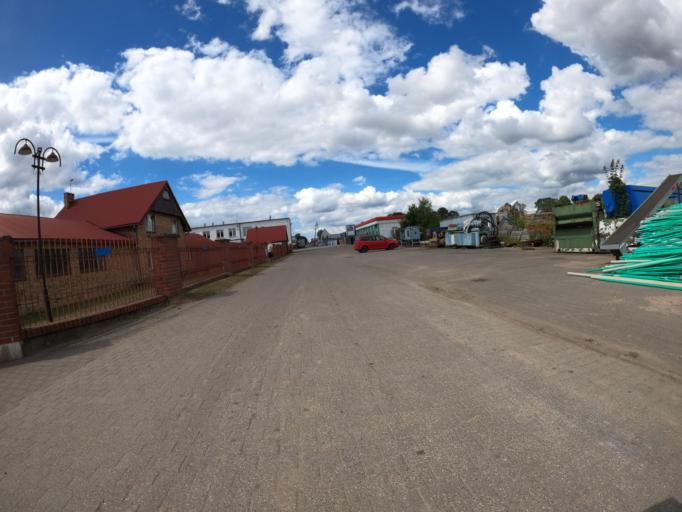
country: PL
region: West Pomeranian Voivodeship
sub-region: Powiat swidwinski
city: Swidwin
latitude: 53.7593
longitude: 15.8130
